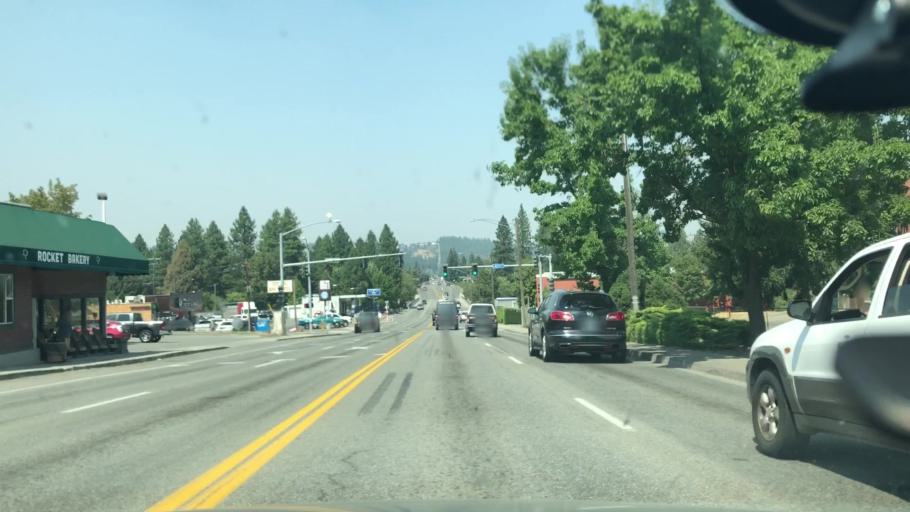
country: US
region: Washington
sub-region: Spokane County
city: Millwood
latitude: 47.6871
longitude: -117.2827
